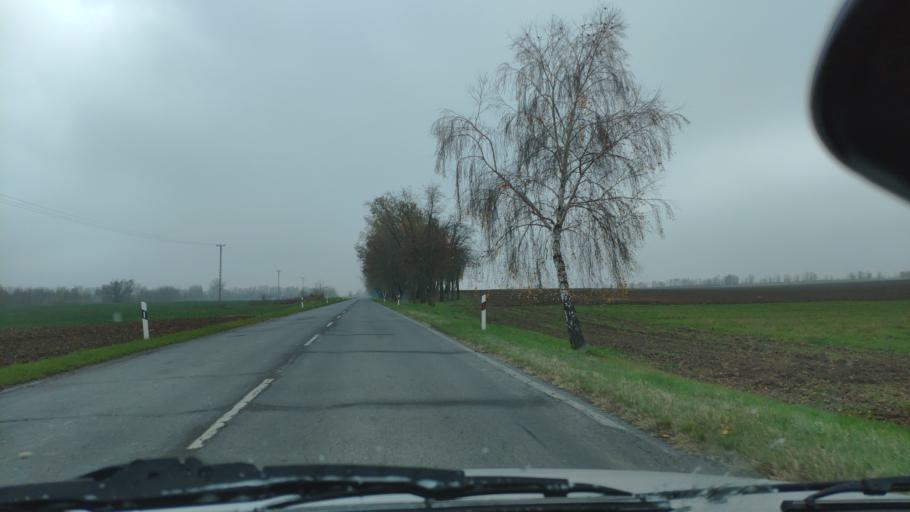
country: HU
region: Zala
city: Zalakomar
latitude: 46.5947
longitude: 17.2634
